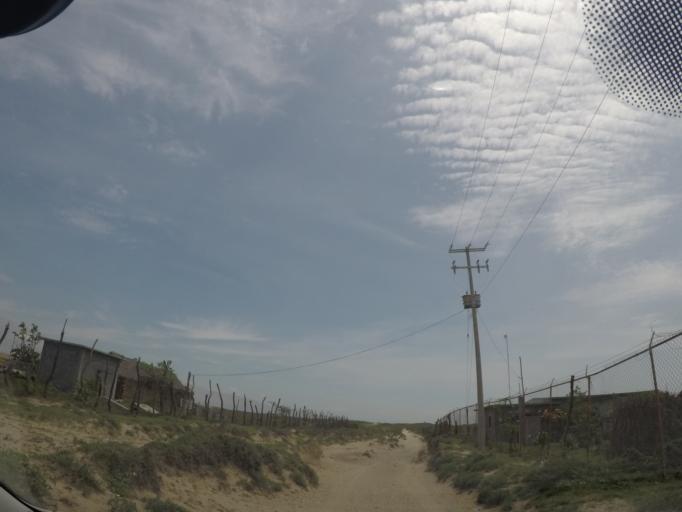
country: MX
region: Oaxaca
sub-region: San Mateo del Mar
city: Colonia Juarez
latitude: 16.2135
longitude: -95.0358
